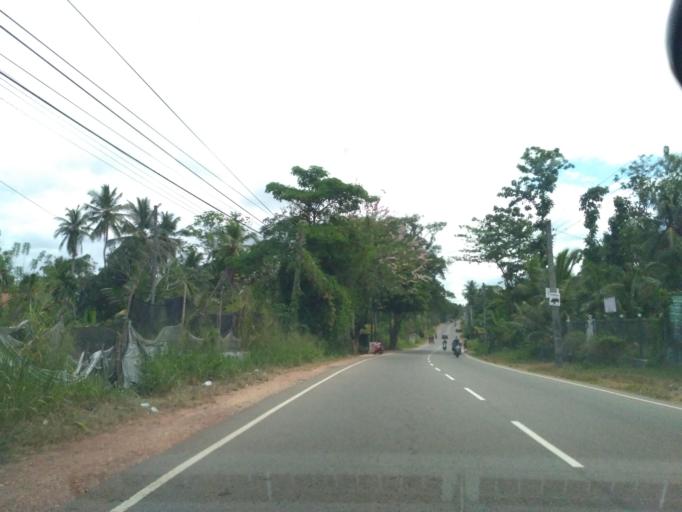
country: LK
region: North Western
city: Kuliyapitiya
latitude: 7.3261
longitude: 80.0448
